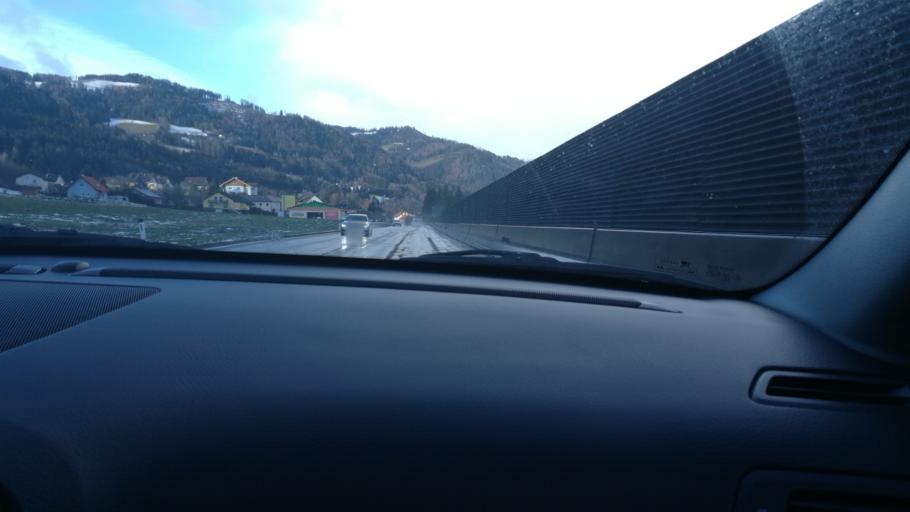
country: AT
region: Styria
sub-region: Politischer Bezirk Murtal
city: Oberweg
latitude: 47.1745
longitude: 14.6158
